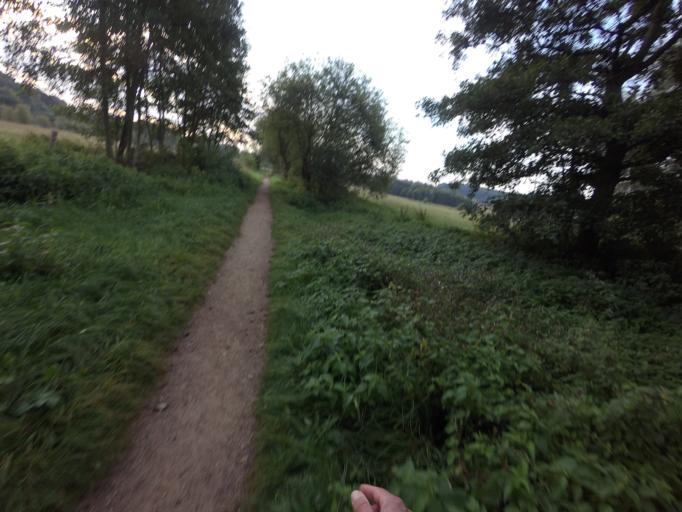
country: NL
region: Limburg
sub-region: Valkenburg aan de Geul
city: Valkenburg
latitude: 50.8587
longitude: 5.8438
